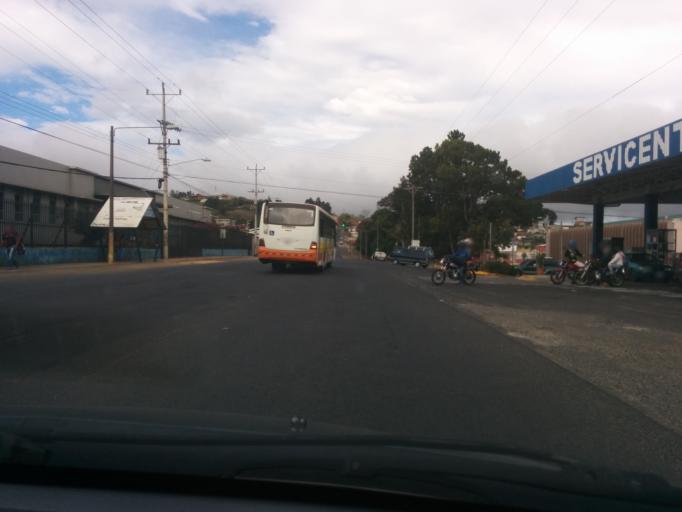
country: CR
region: Alajuela
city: San Ramon
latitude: 10.0823
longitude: -84.4699
